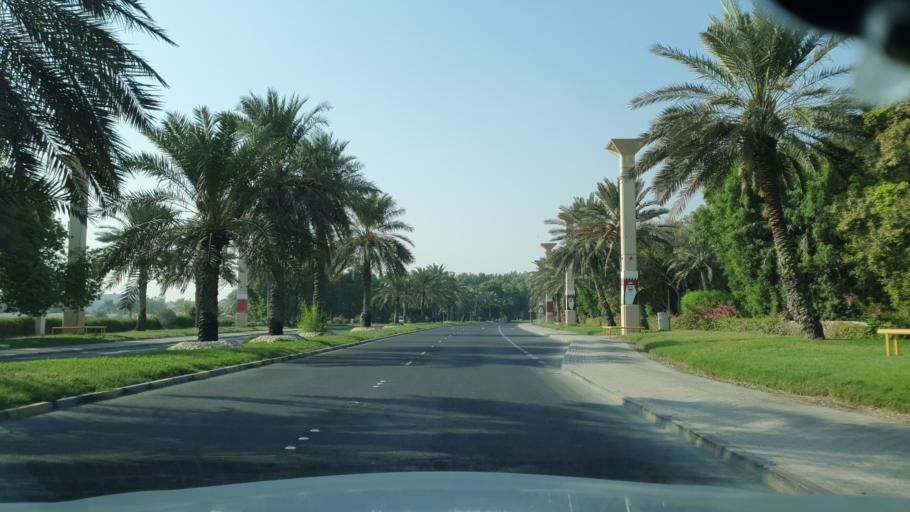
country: BH
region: Northern
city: Ar Rifa'
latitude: 26.1279
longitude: 50.5370
